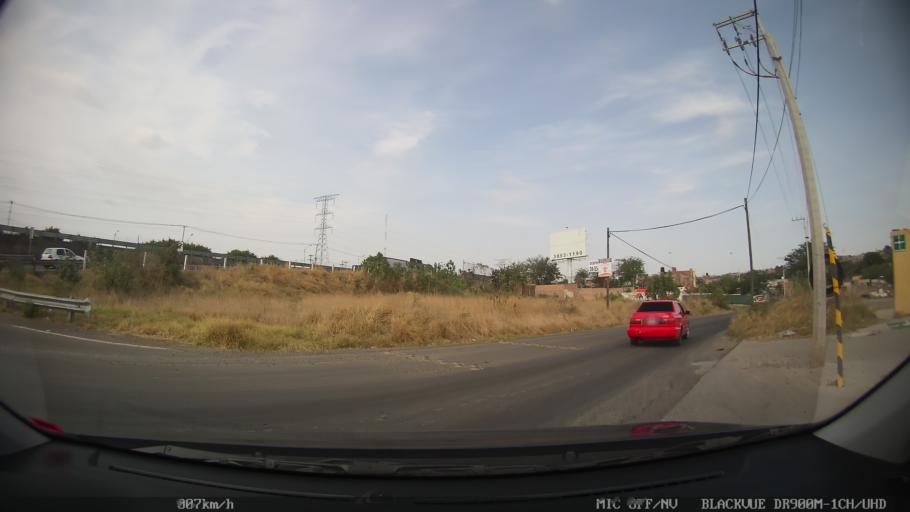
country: MX
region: Jalisco
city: Tonala
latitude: 20.6181
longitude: -103.2269
